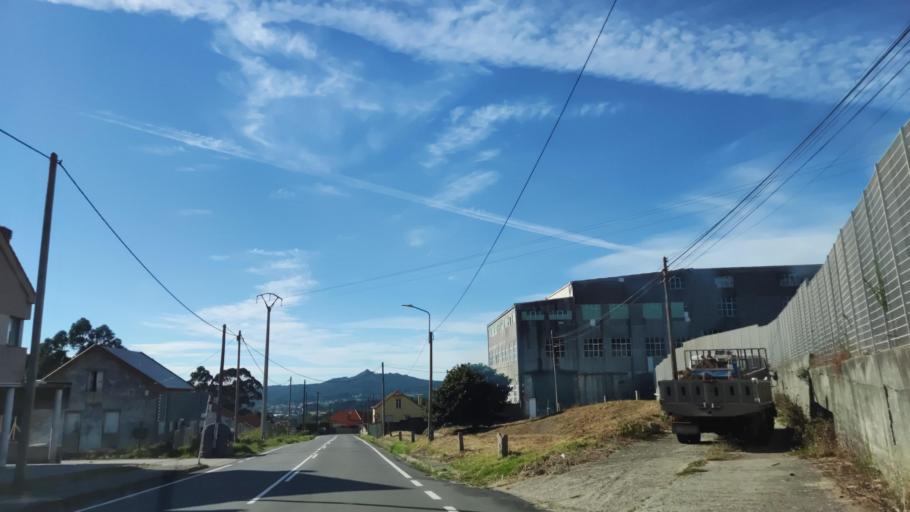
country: ES
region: Galicia
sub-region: Provincia da Coruna
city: Boiro
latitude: 42.5716
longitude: -8.9996
